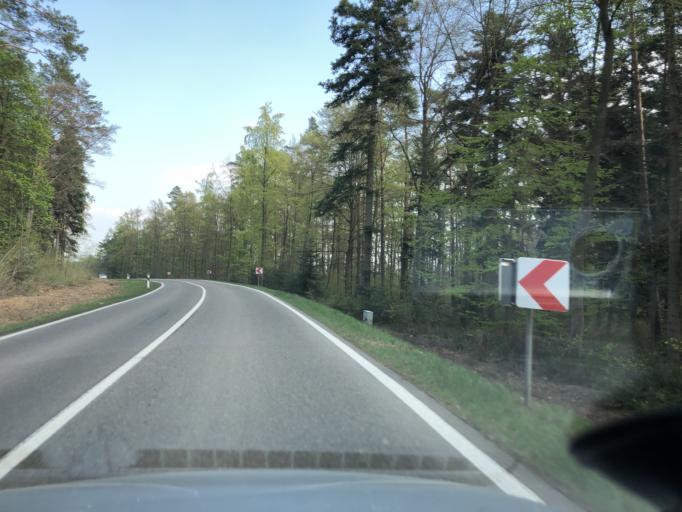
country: DE
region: Baden-Wuerttemberg
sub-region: Regierungsbezirk Stuttgart
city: Weil der Stadt
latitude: 48.7565
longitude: 8.8427
